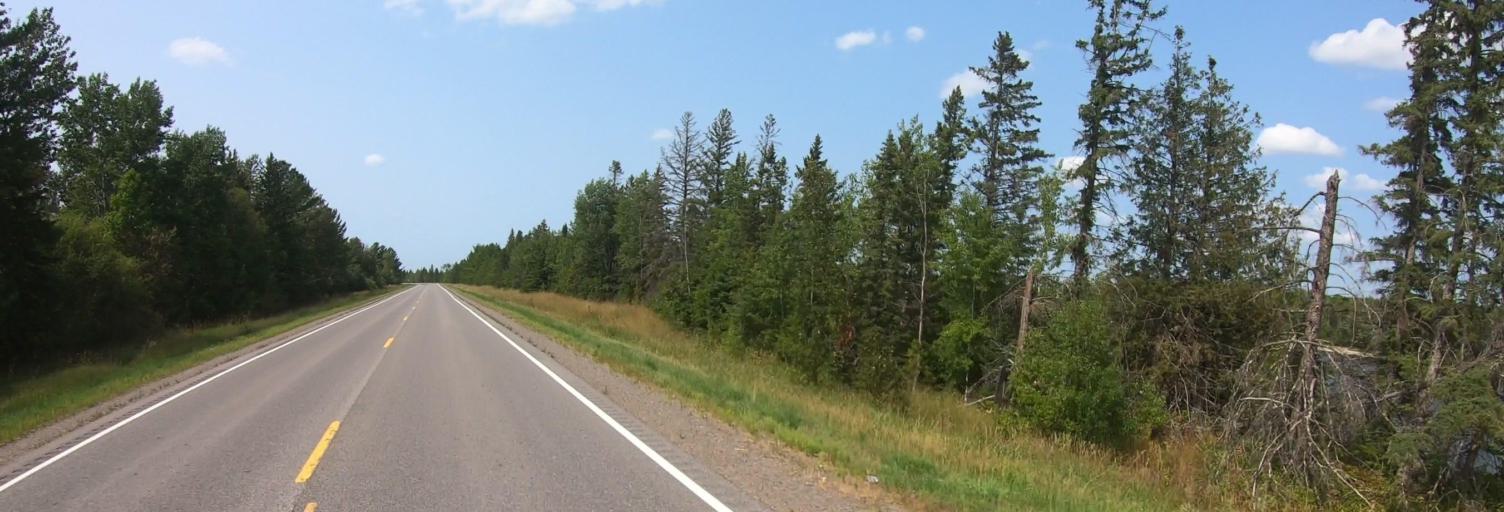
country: US
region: Minnesota
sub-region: Lake of the Woods County
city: Baudette
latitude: 48.6444
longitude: -94.1589
